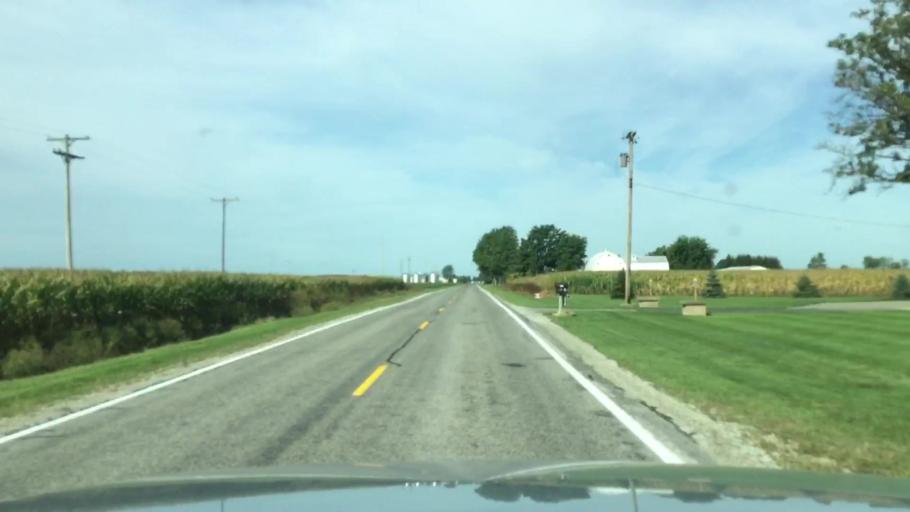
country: US
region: Michigan
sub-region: Genesee County
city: Montrose
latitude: 43.1470
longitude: -83.9567
